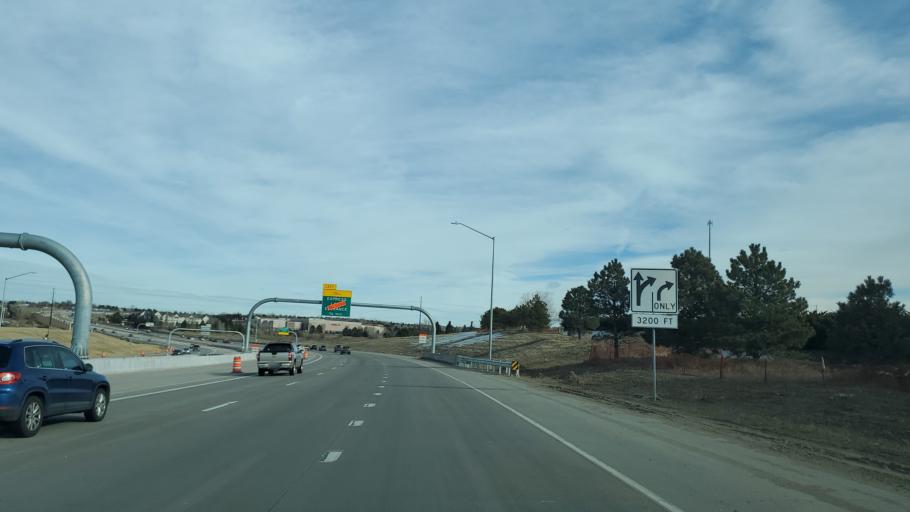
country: US
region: Colorado
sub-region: Douglas County
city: Highlands Ranch
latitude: 39.5585
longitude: -105.0017
